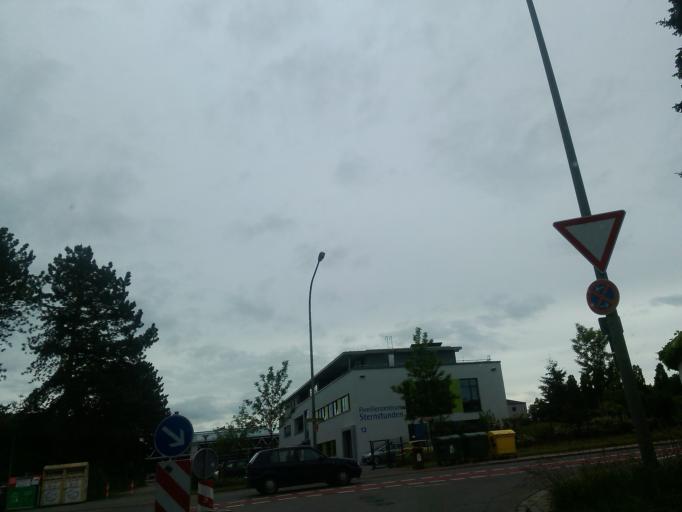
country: DE
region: Bavaria
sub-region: Swabia
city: Augsburg
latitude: 48.3379
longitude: 10.8759
